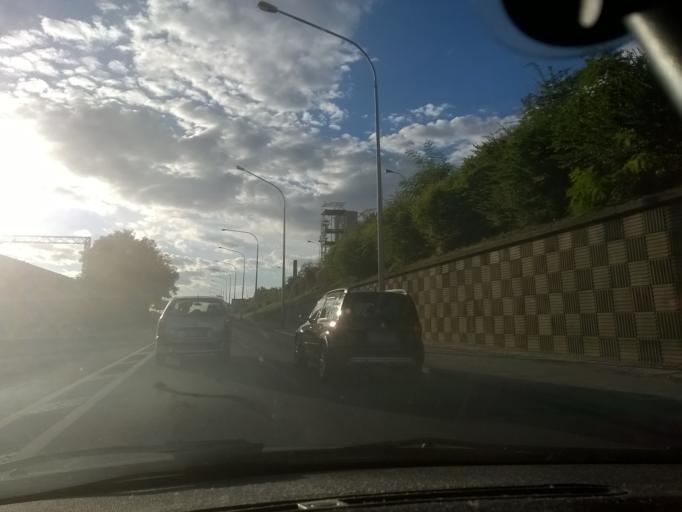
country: HR
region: Grad Zagreb
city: Stenjevec
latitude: 45.8146
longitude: 15.8593
